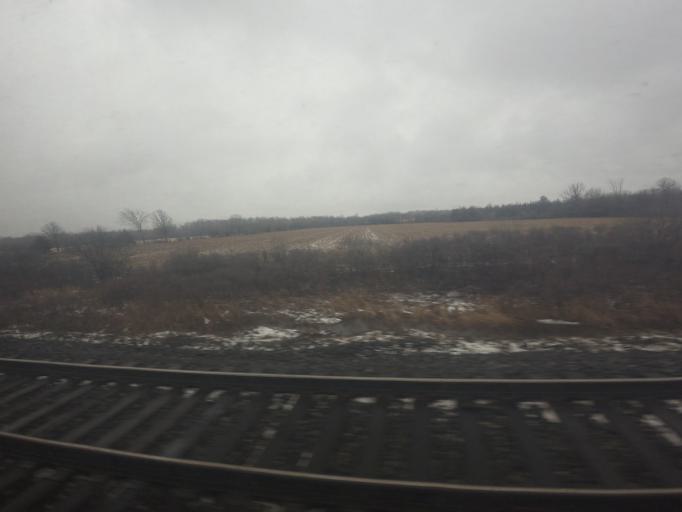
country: CA
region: Ontario
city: Deseronto
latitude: 44.2169
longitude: -77.1655
